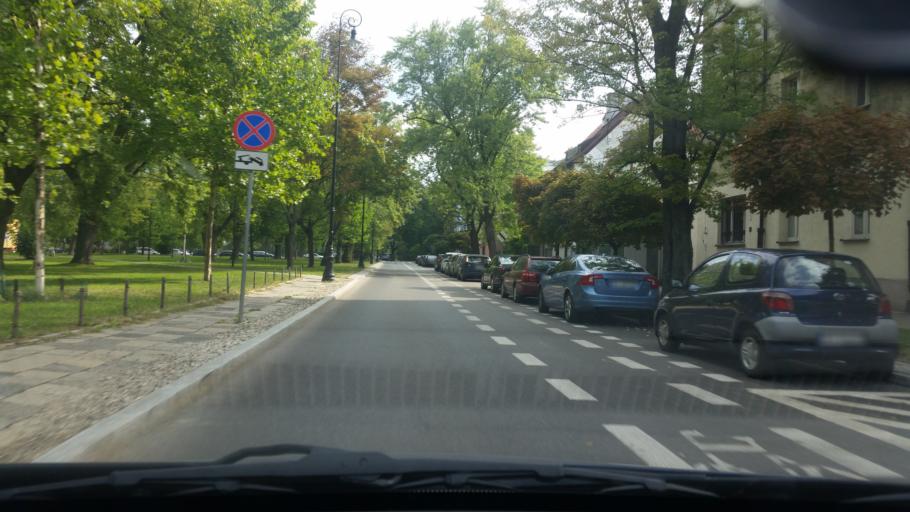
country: PL
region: Masovian Voivodeship
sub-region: Warszawa
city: Zoliborz
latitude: 52.2634
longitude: 20.9876
